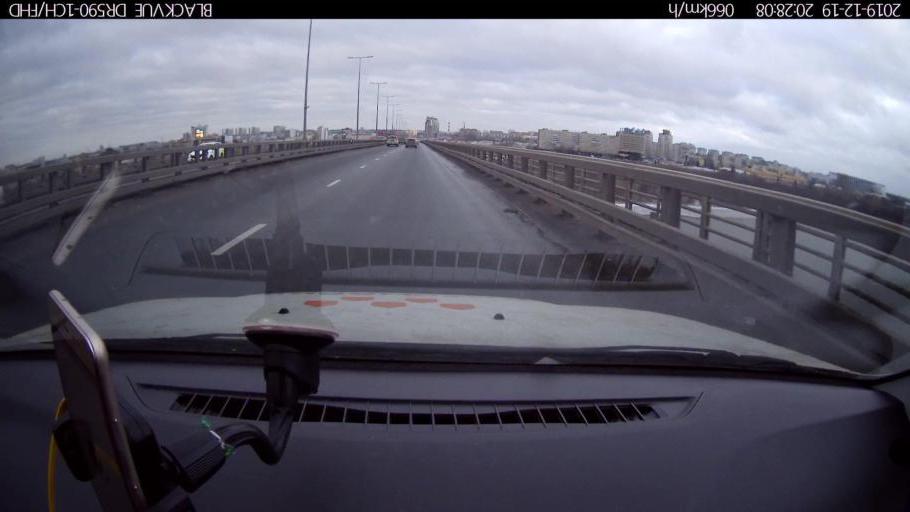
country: RU
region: Nizjnij Novgorod
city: Nizhniy Novgorod
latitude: 56.3193
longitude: 43.9655
